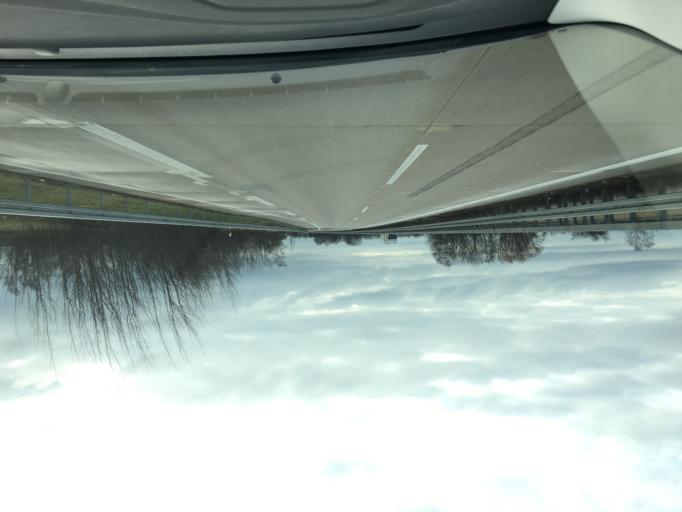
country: DE
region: Saxony
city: Grossweitzschen
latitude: 51.1875
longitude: 13.0134
